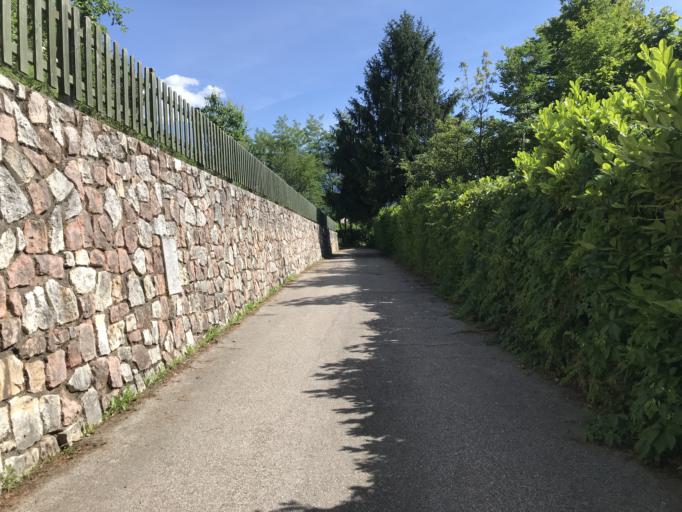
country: IT
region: Trentino-Alto Adige
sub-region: Provincia di Trento
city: Povo
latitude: 46.0619
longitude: 11.1402
